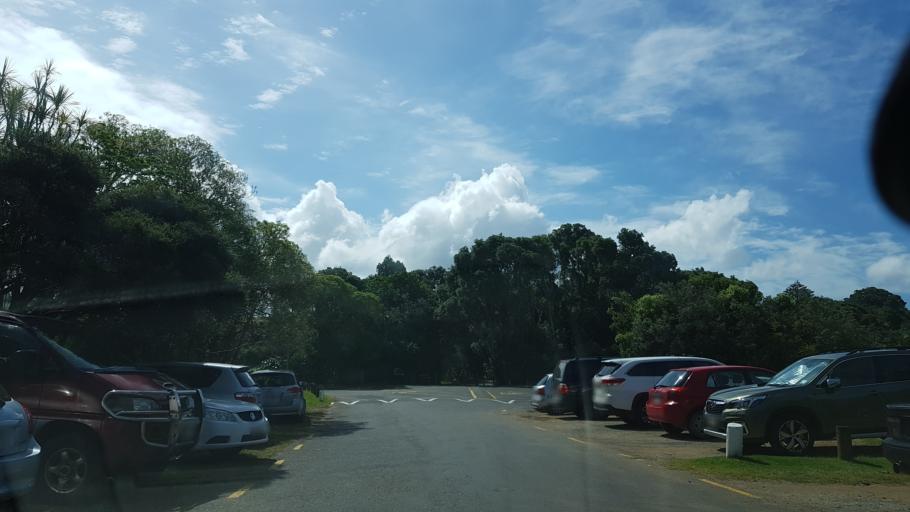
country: NZ
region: Auckland
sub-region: Auckland
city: Rothesay Bay
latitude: -36.6826
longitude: 174.7473
